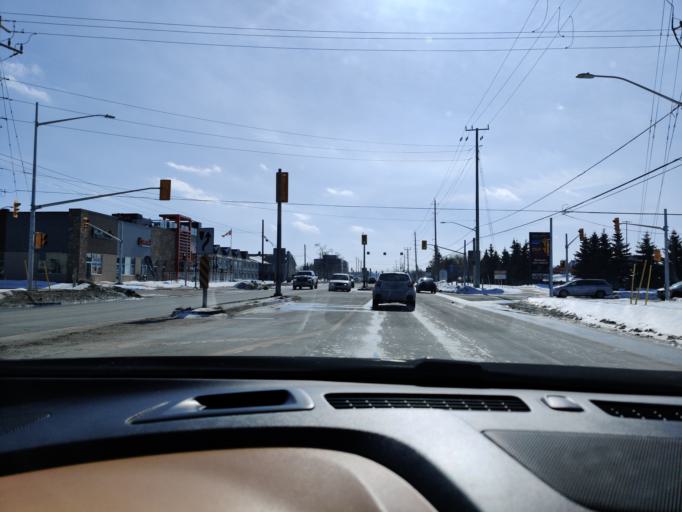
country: CA
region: Ontario
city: Collingwood
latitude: 44.5034
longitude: -80.2350
